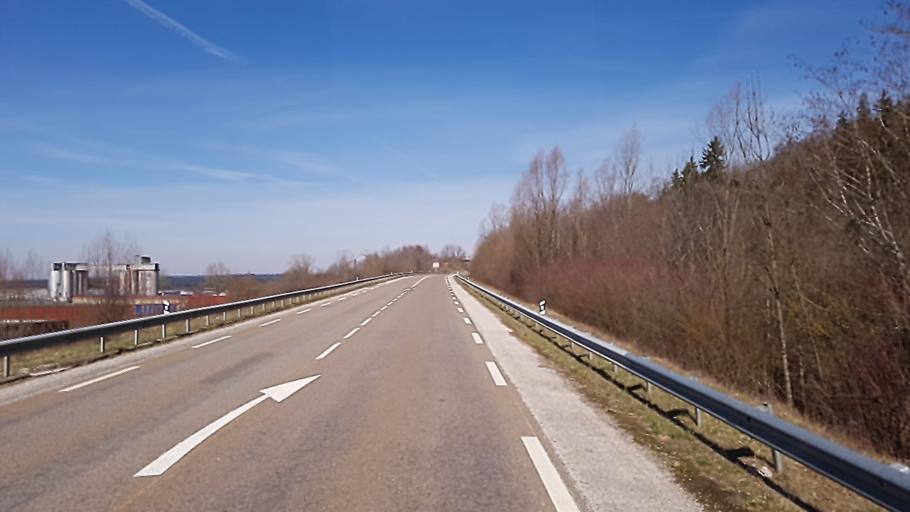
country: FR
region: Franche-Comte
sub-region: Departement du Jura
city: Champagnole
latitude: 46.7512
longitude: 5.9184
